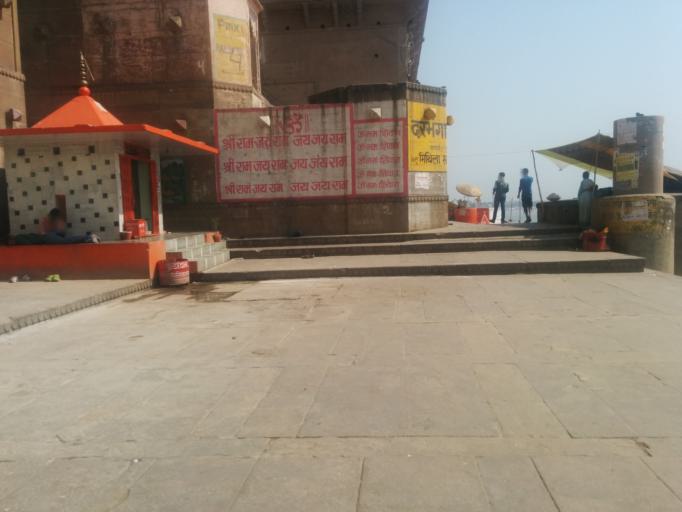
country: IN
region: Uttar Pradesh
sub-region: Varanasi
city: Varanasi
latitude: 25.3053
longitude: 83.0097
